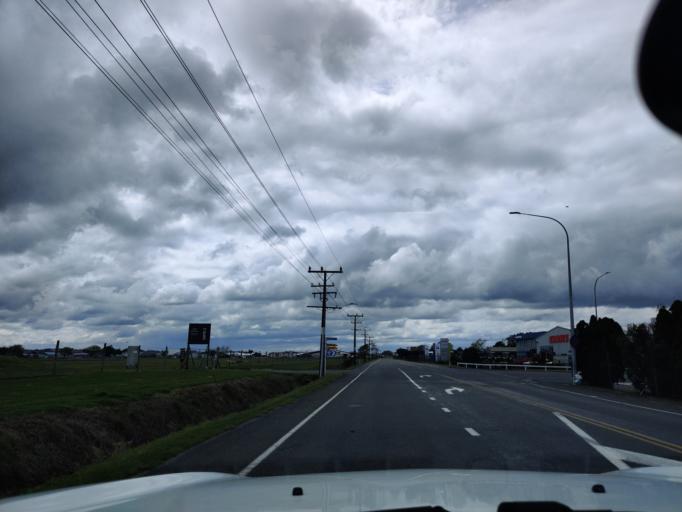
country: NZ
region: Manawatu-Wanganui
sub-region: Palmerston North City
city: Palmerston North
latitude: -40.2356
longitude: 175.5640
